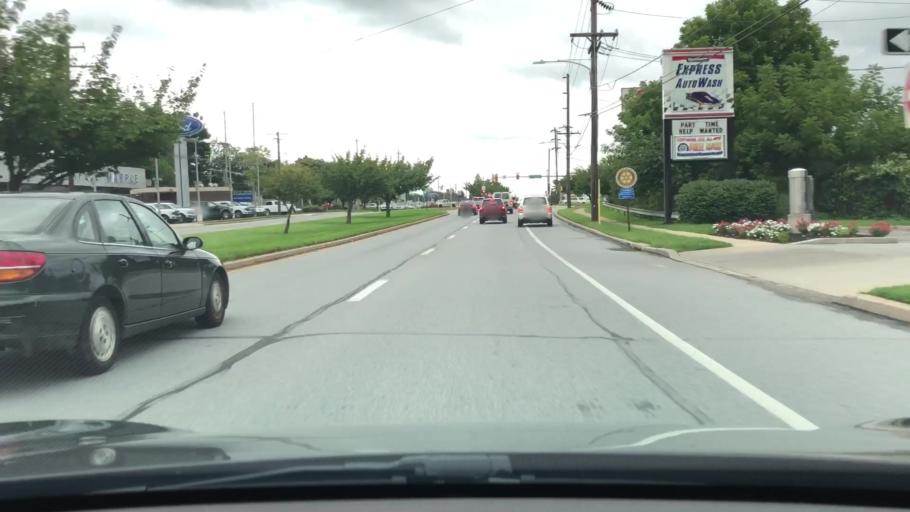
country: US
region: Pennsylvania
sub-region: Delaware County
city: Broomall
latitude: 39.9838
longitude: -75.3759
